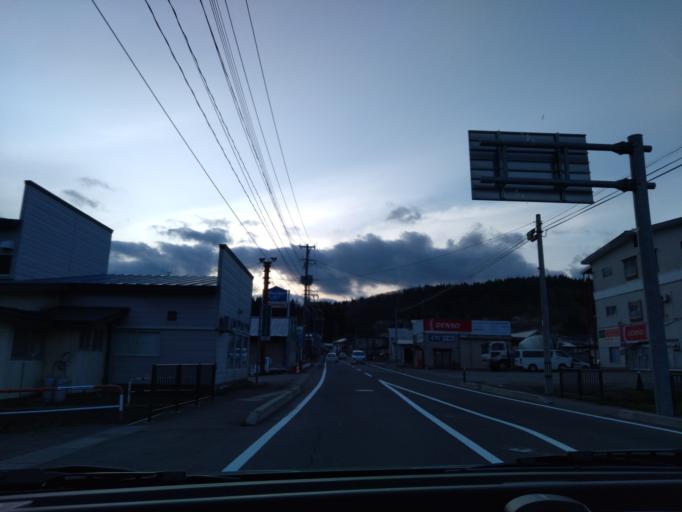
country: JP
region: Akita
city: Kakunodatemachi
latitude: 39.5944
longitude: 140.5762
